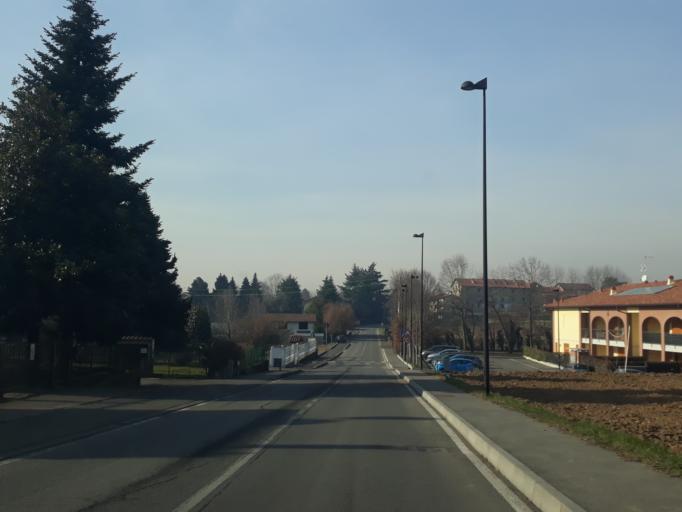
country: IT
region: Lombardy
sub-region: Provincia di Monza e Brianza
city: Bellusco
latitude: 45.6231
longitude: 9.4104
